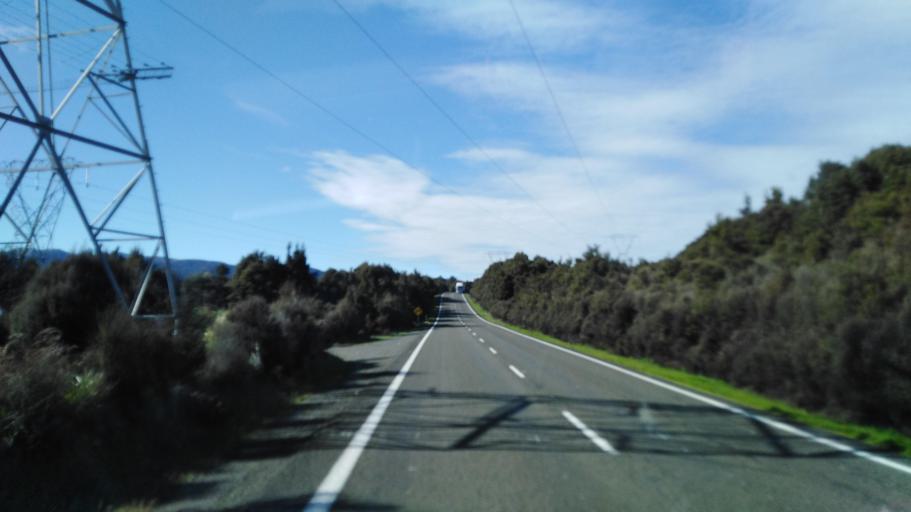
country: NZ
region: Waikato
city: Turangi
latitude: -39.2004
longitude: 175.7566
